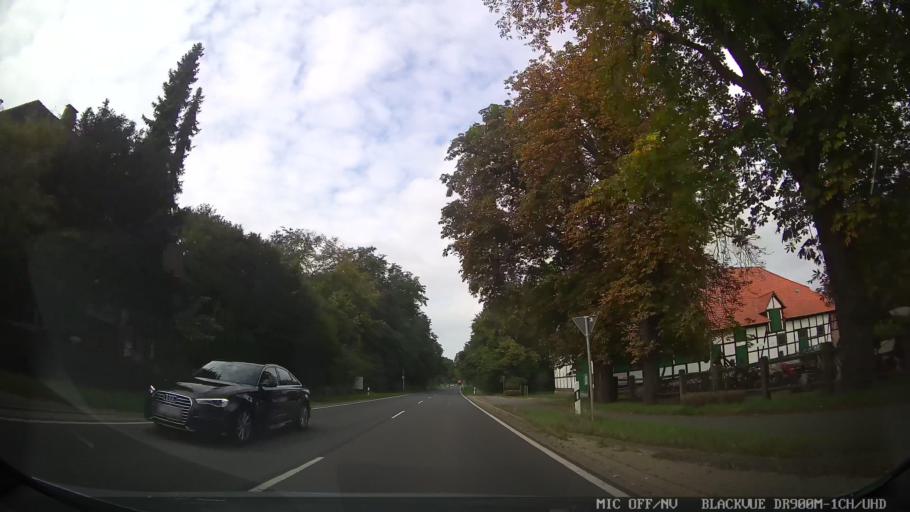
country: DE
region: Lower Saxony
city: Klein Schwulper
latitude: 52.3170
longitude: 10.4519
